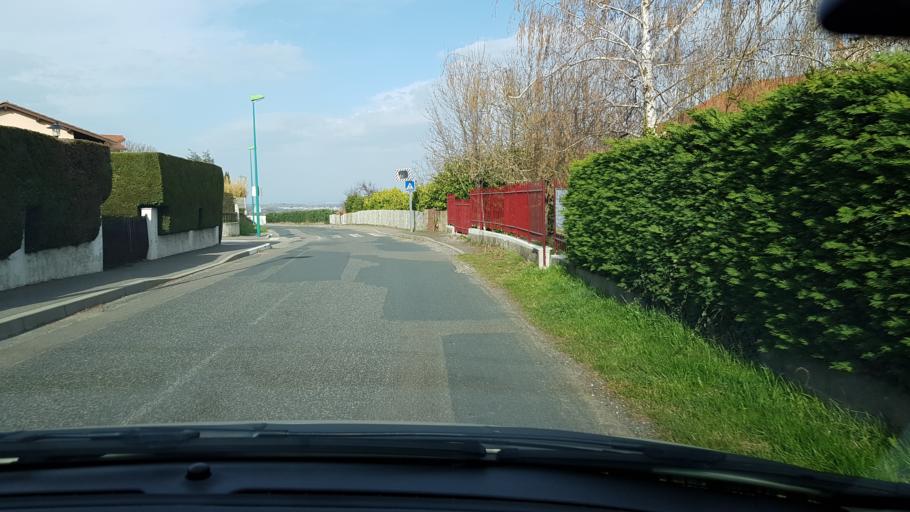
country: FR
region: Rhone-Alpes
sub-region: Departement du Rhone
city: Saint-Maurice-sur-Dargoire
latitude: 45.5816
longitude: 4.6344
